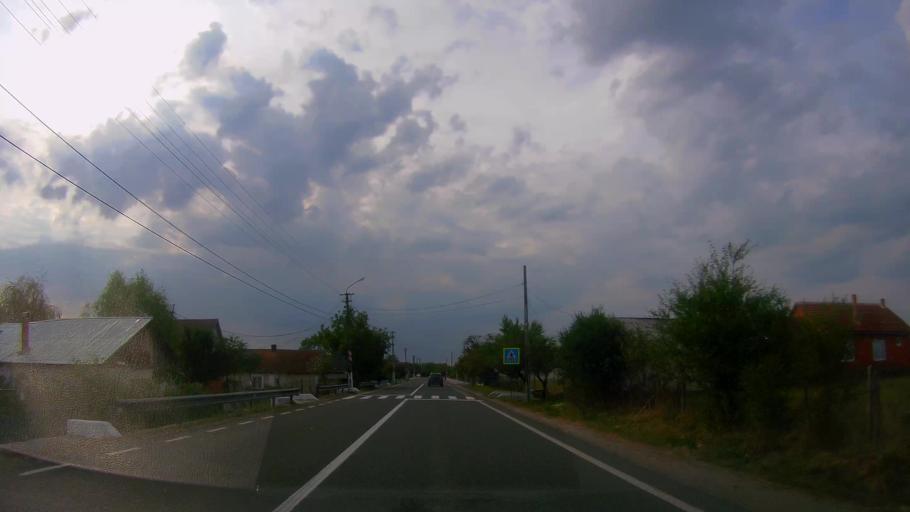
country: RO
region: Satu Mare
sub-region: Oras Ardud
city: Ardud
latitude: 47.5947
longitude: 22.8796
